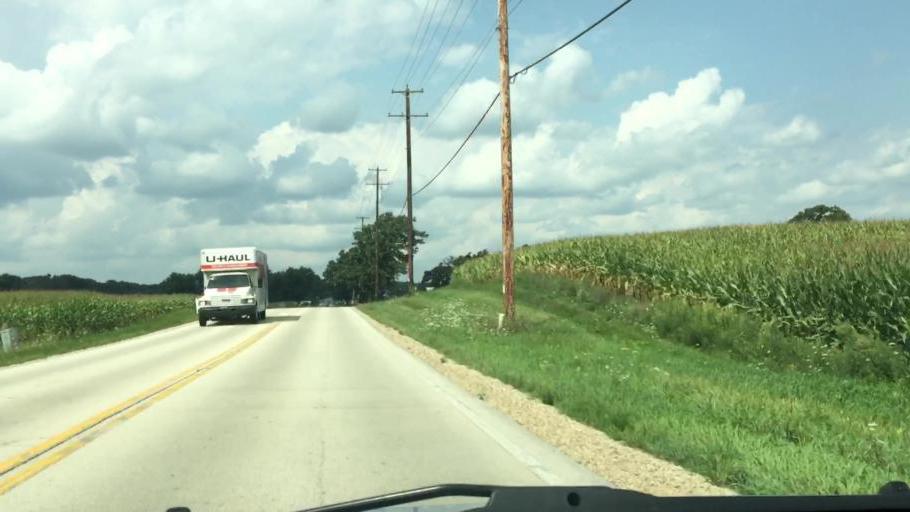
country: US
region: Wisconsin
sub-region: Waukesha County
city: North Prairie
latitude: 42.9411
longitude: -88.4055
